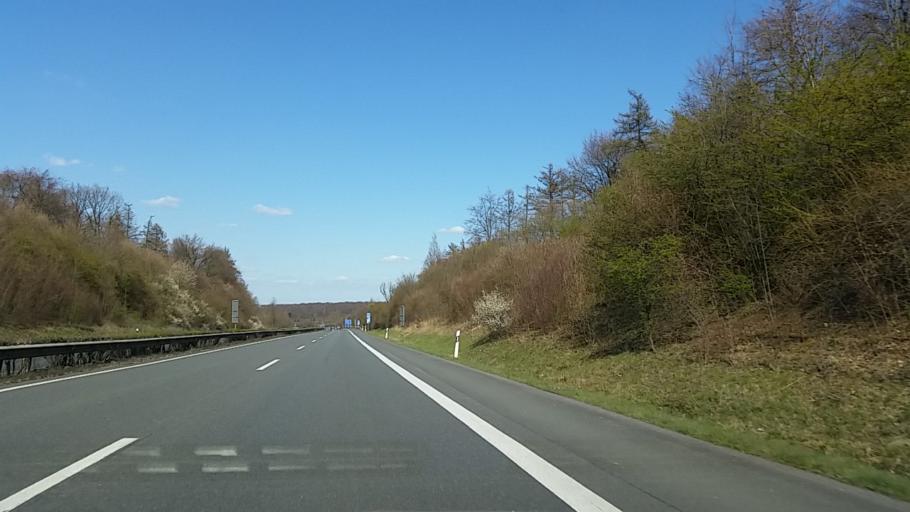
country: DE
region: Lower Saxony
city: Cramme
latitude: 52.1316
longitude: 10.4894
